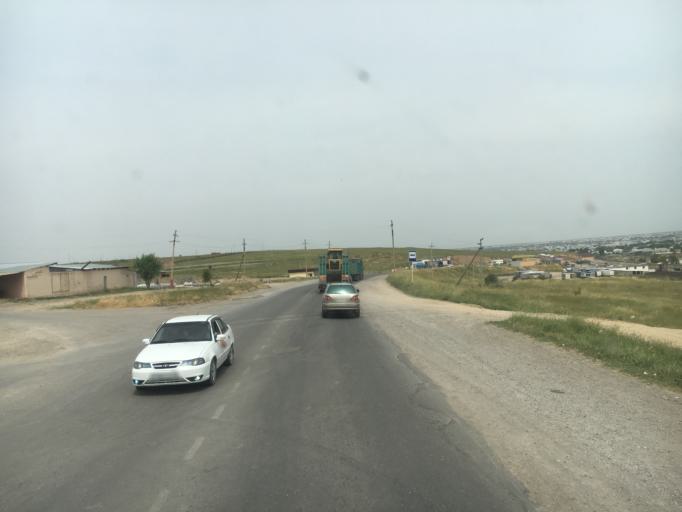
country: KZ
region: Ongtustik Qazaqstan
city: Shymkent
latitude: 42.3236
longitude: 69.5153
